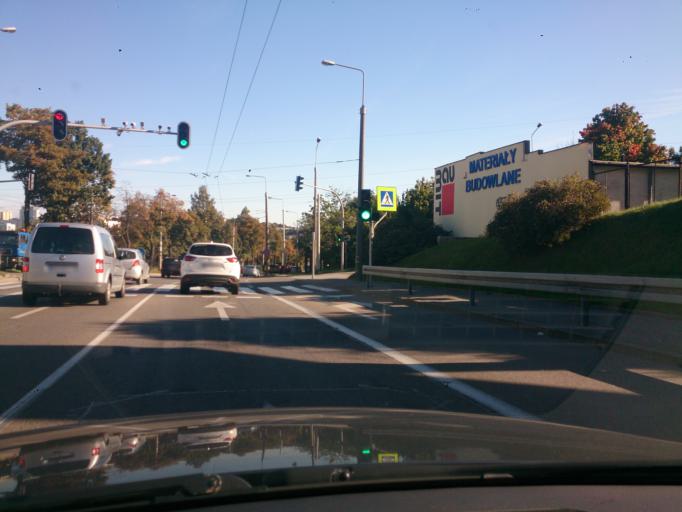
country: PL
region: Pomeranian Voivodeship
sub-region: Gdynia
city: Gdynia
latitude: 54.4812
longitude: 18.5314
